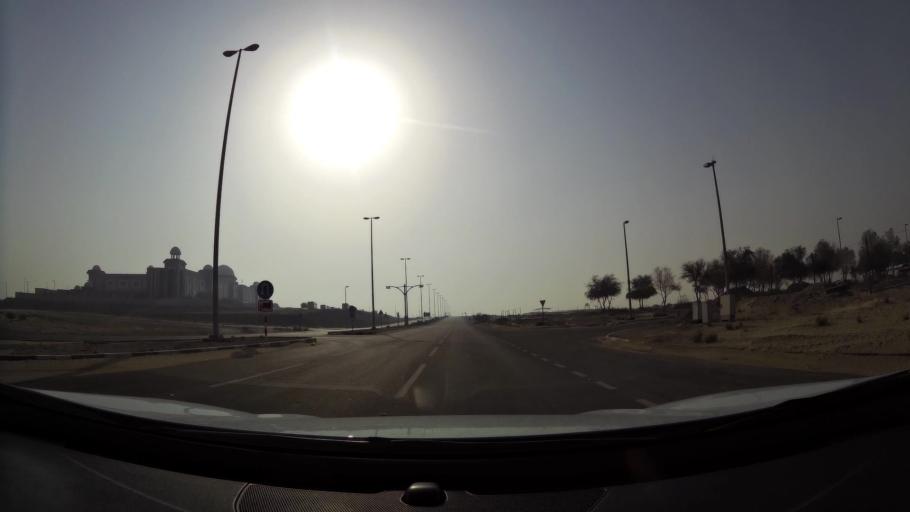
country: AE
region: Abu Dhabi
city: Abu Dhabi
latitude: 24.2709
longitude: 54.6484
